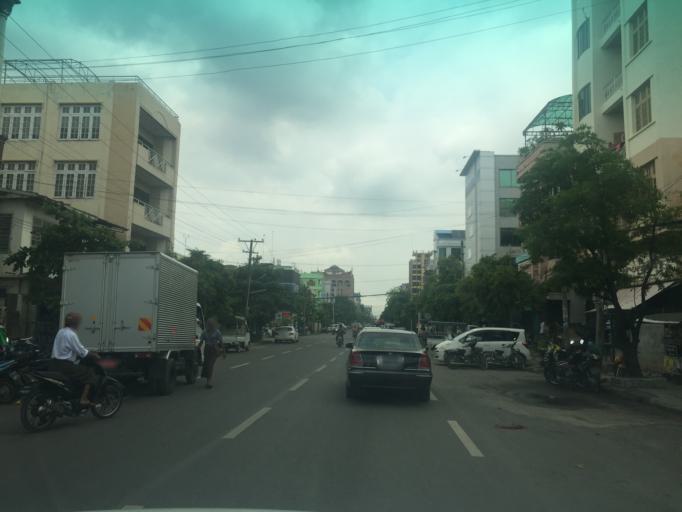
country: MM
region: Mandalay
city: Mandalay
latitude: 21.9704
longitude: 96.0788
